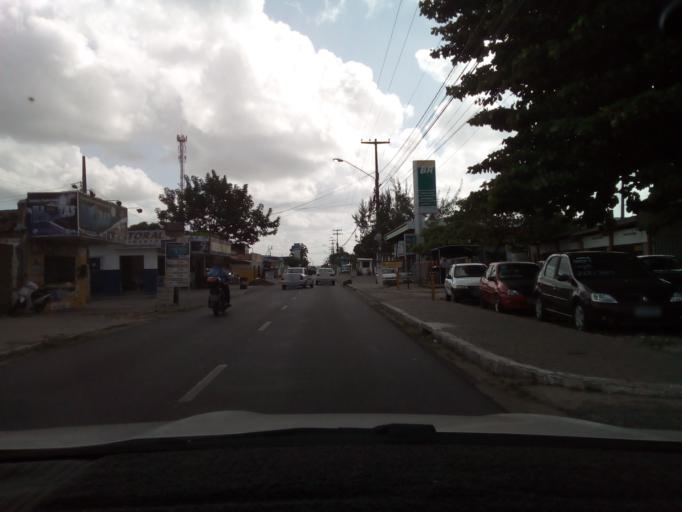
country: BR
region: Paraiba
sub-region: Bayeux
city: Bayeux
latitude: -7.1221
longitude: -34.9128
